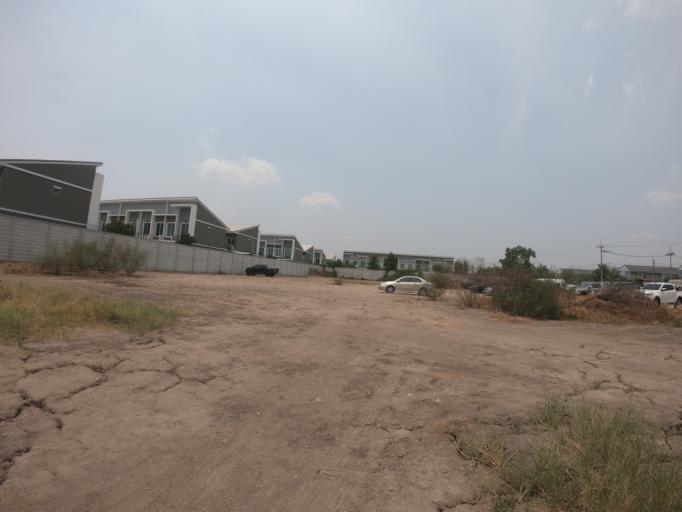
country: TH
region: Phra Nakhon Si Ayutthaya
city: Ban Bang Kadi Pathum Thani
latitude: 14.0075
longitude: 100.5686
